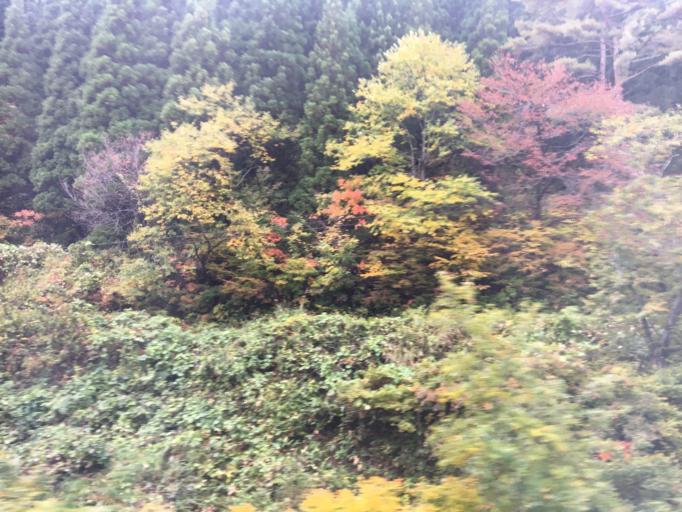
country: JP
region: Yamagata
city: Nagai
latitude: 38.0150
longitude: 139.8977
